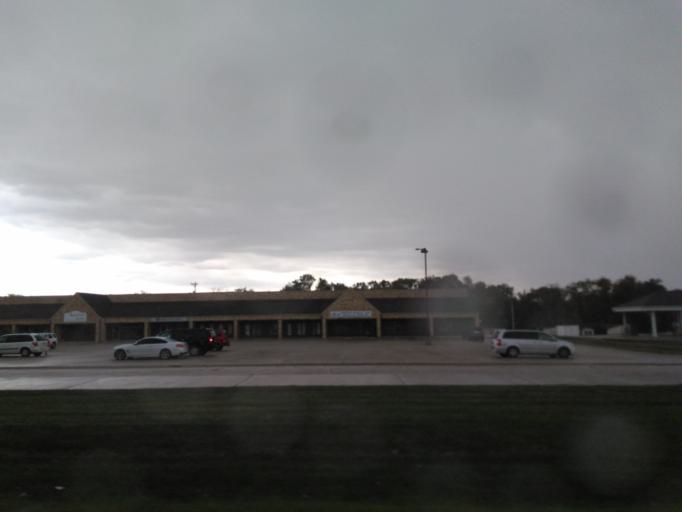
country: US
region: Illinois
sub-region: Madison County
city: Highland
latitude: 38.7492
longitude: -89.6764
